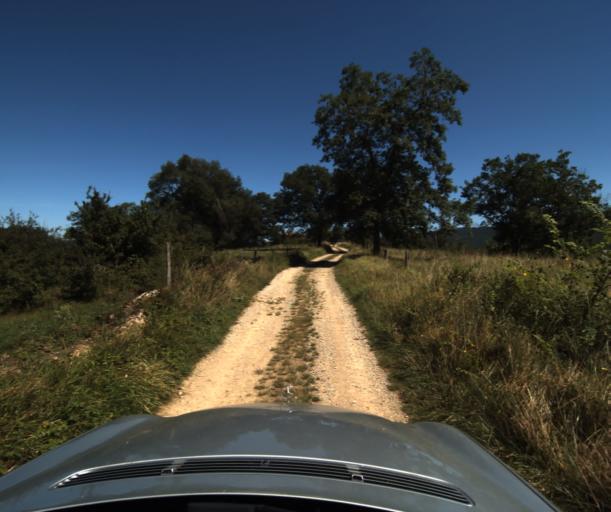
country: FR
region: Midi-Pyrenees
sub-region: Departement de l'Ariege
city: Belesta
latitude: 42.9636
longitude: 1.9259
